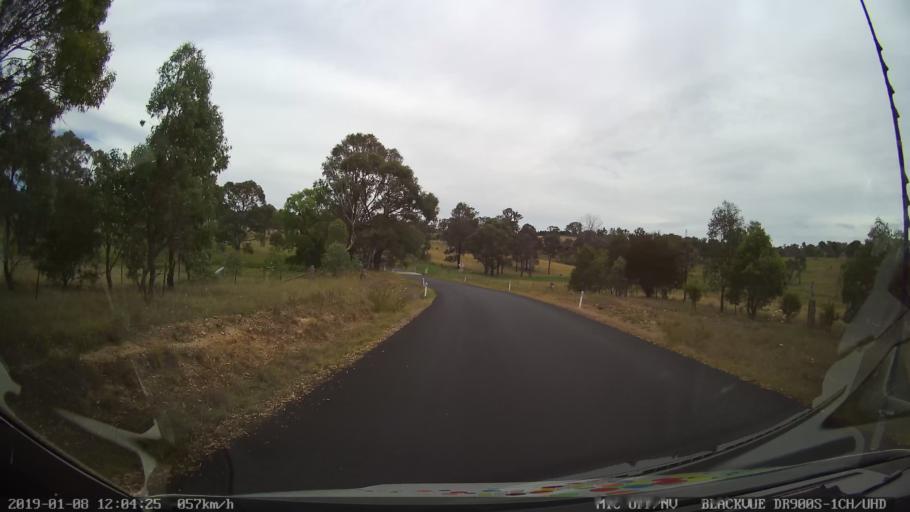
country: AU
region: New South Wales
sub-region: Armidale Dumaresq
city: Armidale
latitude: -30.4433
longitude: 151.5900
